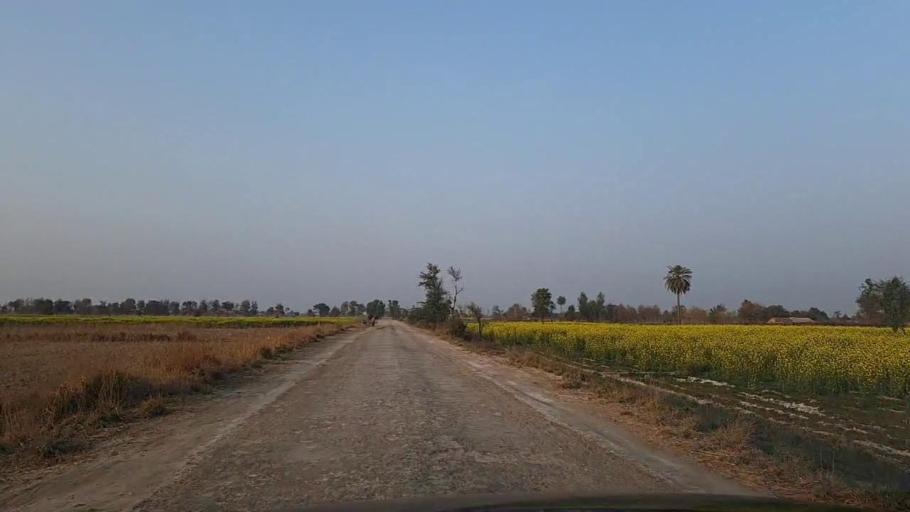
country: PK
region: Sindh
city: Daur
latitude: 26.4267
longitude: 68.3859
